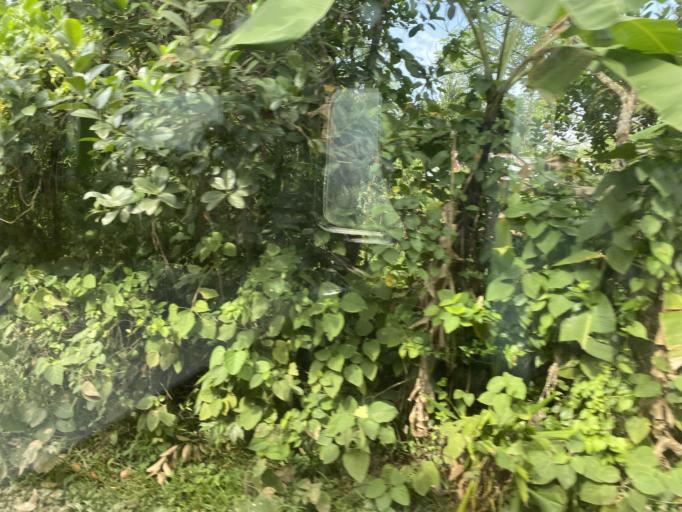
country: IN
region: Tripura
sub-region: West Tripura
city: Agartala
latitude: 23.9866
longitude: 91.2829
